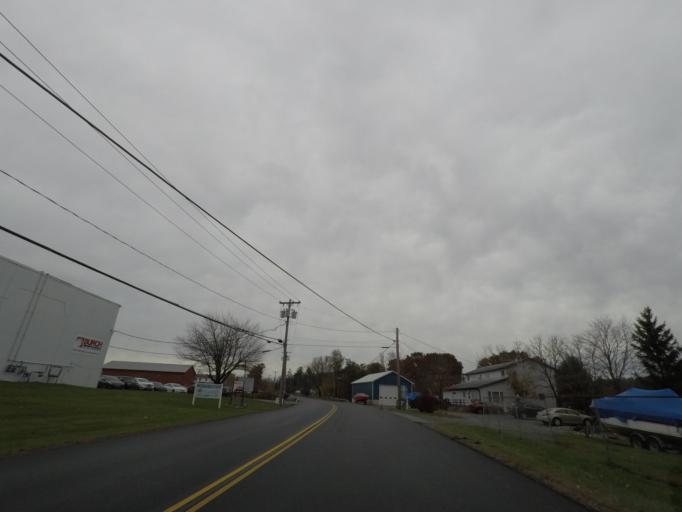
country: US
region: New York
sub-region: Saratoga County
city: Waterford
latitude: 42.8285
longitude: -73.6671
